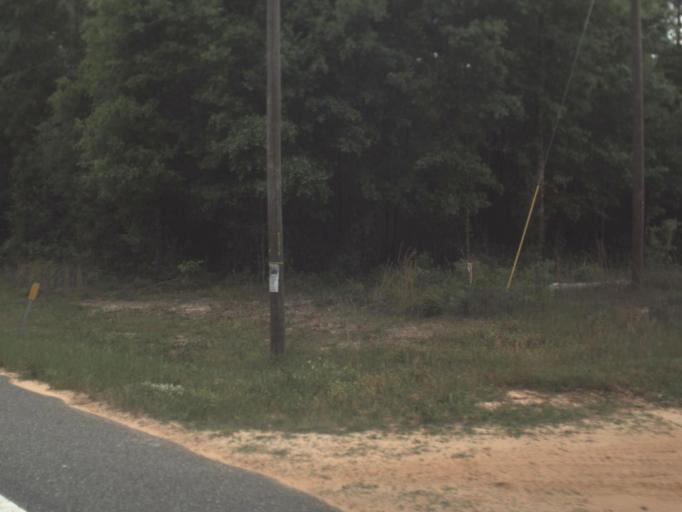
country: US
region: Florida
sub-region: Santa Rosa County
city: Point Baker
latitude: 30.7226
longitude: -87.0448
